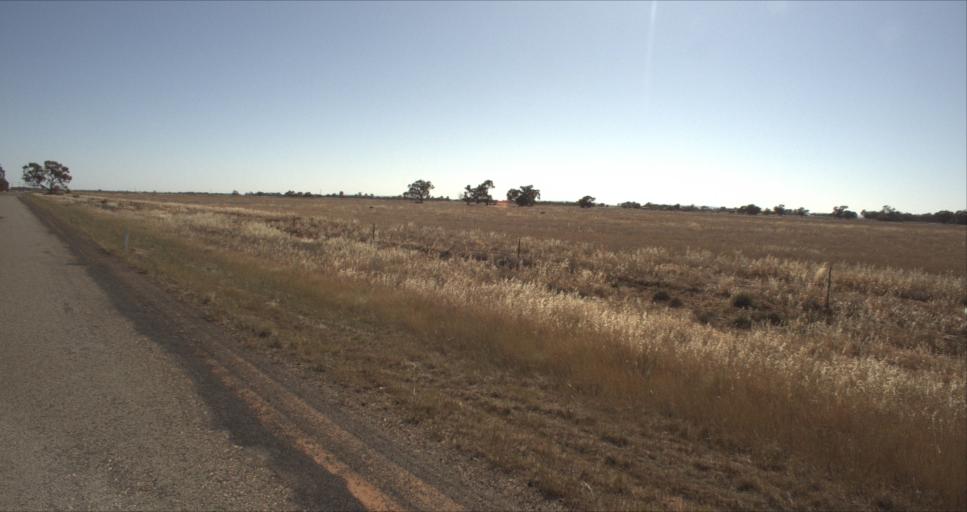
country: AU
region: New South Wales
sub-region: Leeton
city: Leeton
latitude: -34.5591
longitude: 146.2658
